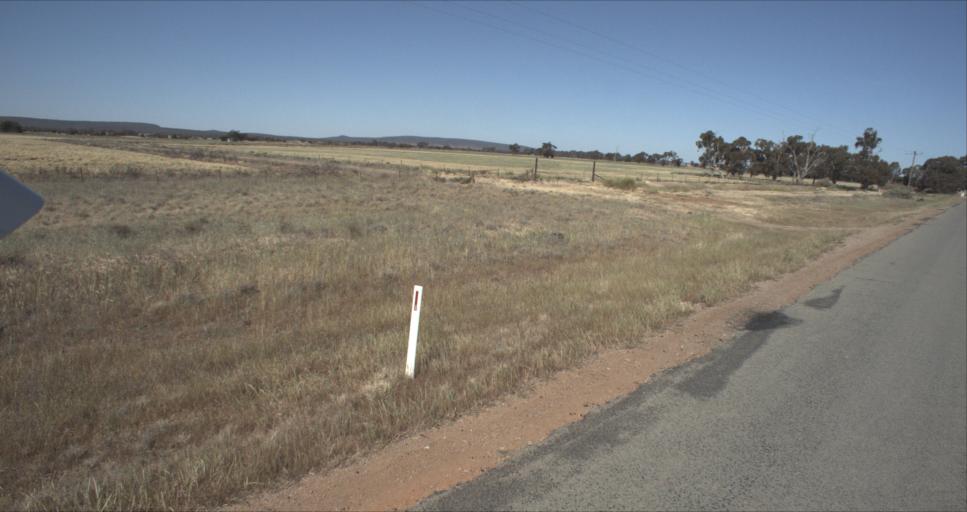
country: AU
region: New South Wales
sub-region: Leeton
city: Leeton
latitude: -34.4981
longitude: 146.3918
